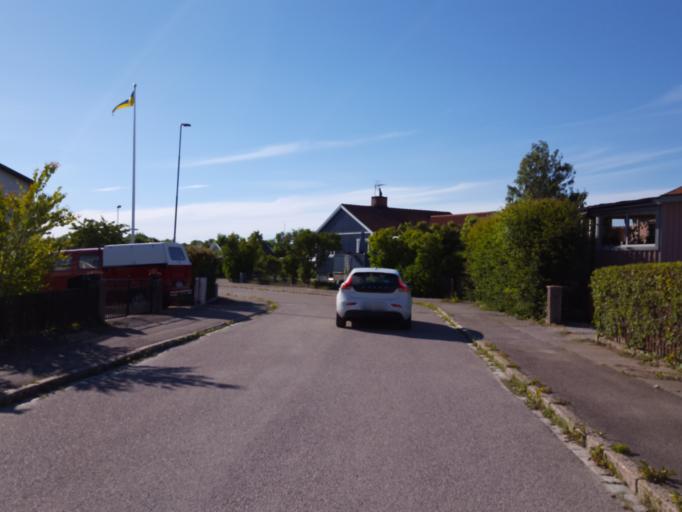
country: SE
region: Uppsala
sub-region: Uppsala Kommun
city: Uppsala
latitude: 59.8619
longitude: 17.6699
